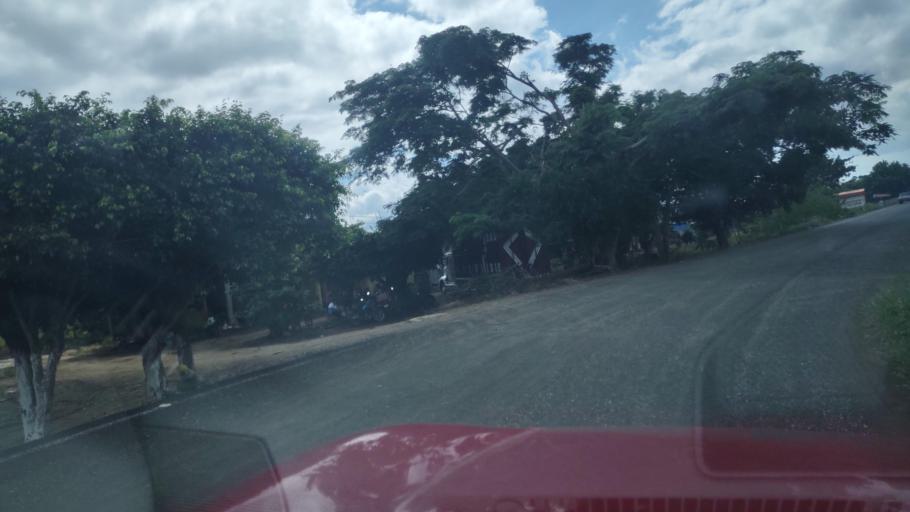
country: MX
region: Puebla
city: San Jose Acateno
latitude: 20.2762
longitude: -97.1298
